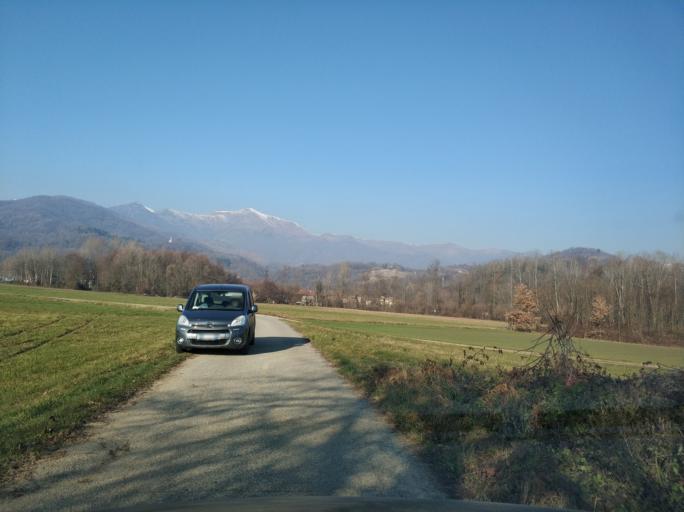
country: IT
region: Piedmont
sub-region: Provincia di Torino
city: Levone
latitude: 45.3132
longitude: 7.6143
